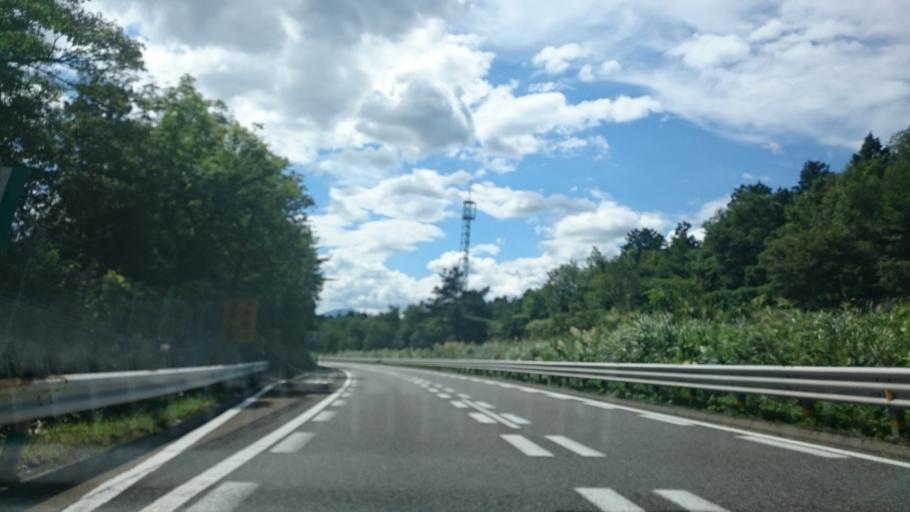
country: JP
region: Gifu
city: Nakatsugawa
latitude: 35.5094
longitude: 137.5439
